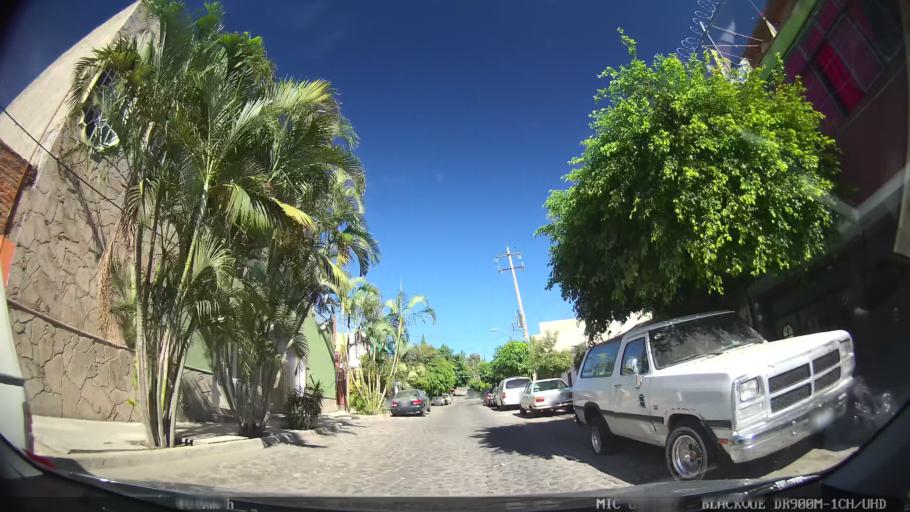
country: MX
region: Jalisco
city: Tlaquepaque
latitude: 20.6893
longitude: -103.2742
